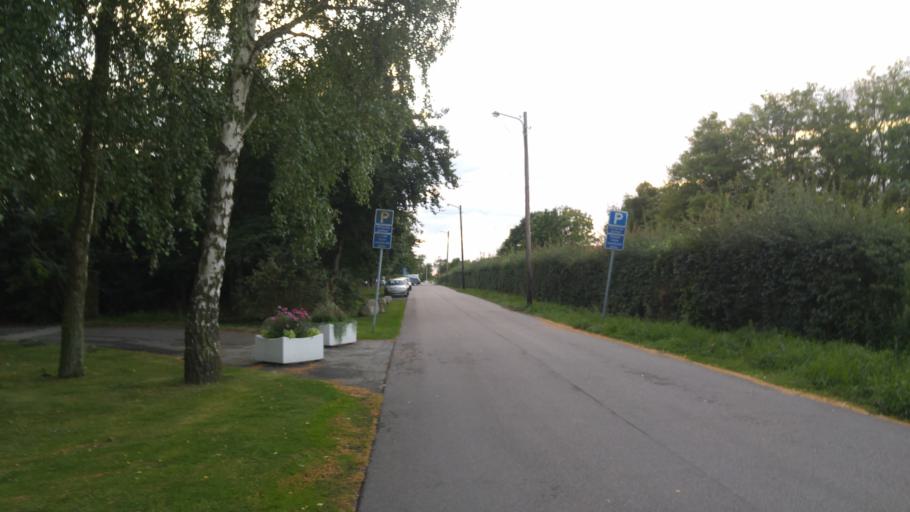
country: SE
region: Skane
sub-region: Malmo
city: Bunkeflostrand
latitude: 55.5660
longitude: 12.9535
